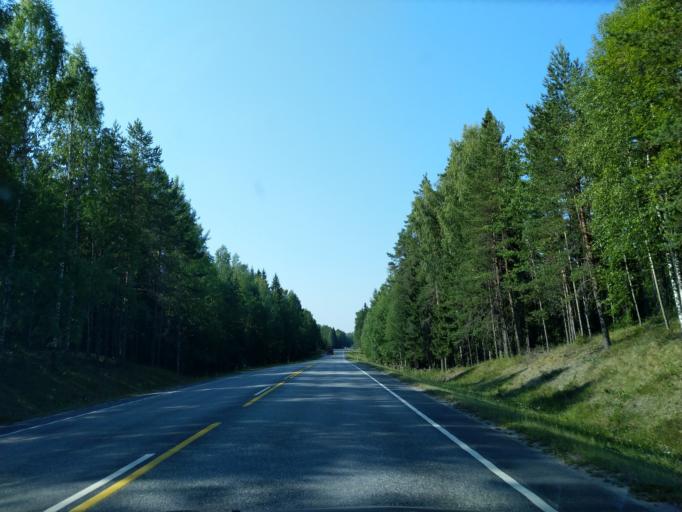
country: FI
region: Satakunta
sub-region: Pori
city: Pomarkku
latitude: 61.6457
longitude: 21.9518
